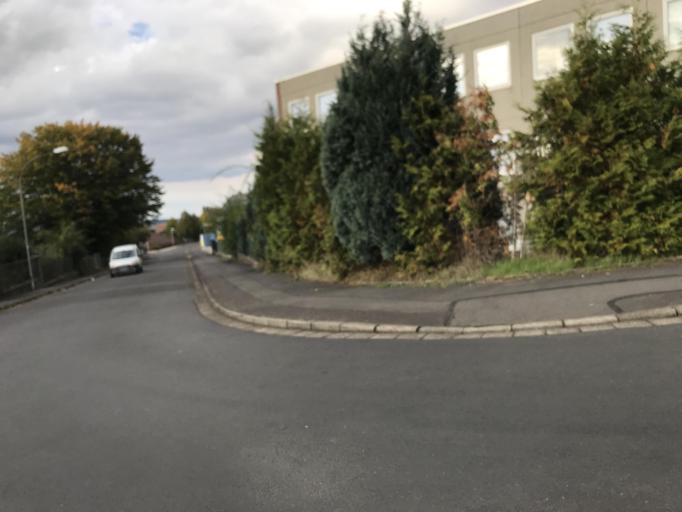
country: DE
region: Hesse
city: Borken
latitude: 51.0441
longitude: 9.2801
